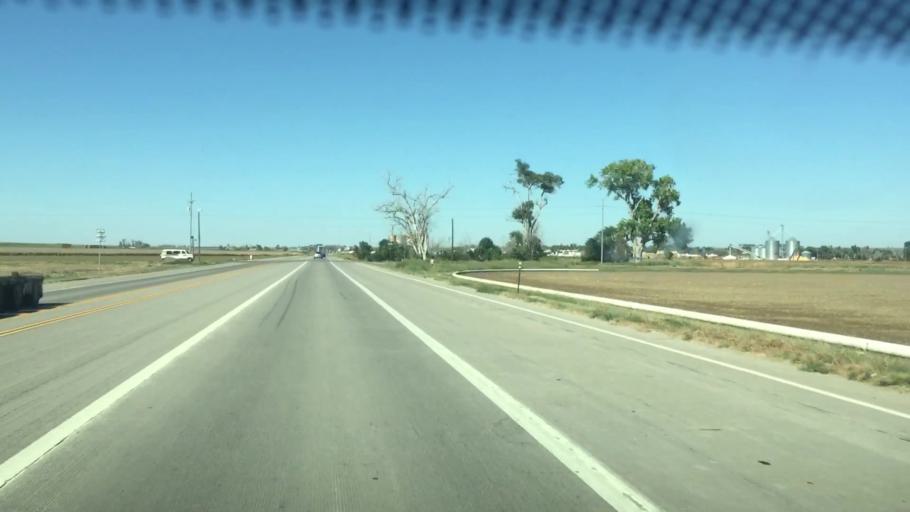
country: US
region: Colorado
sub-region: Prowers County
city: Lamar
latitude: 38.1418
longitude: -102.7237
